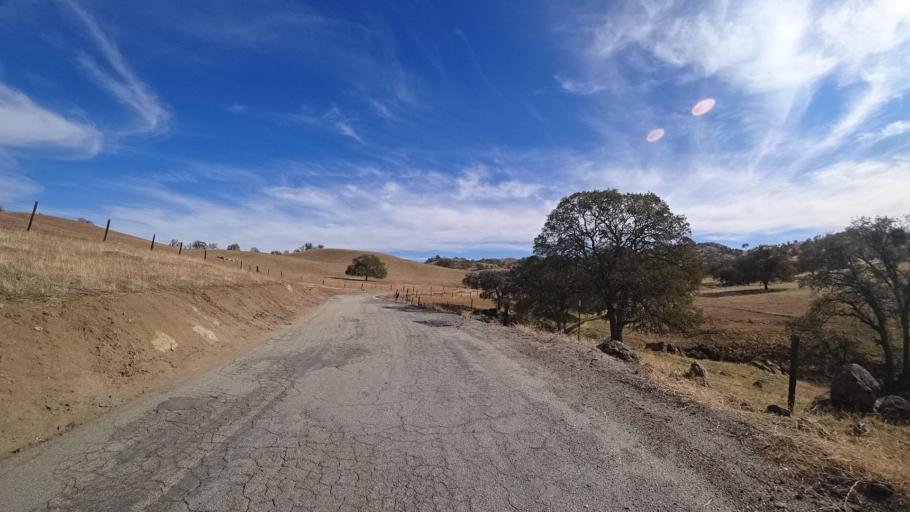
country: US
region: California
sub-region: Kern County
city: Oildale
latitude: 35.5748
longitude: -118.8089
